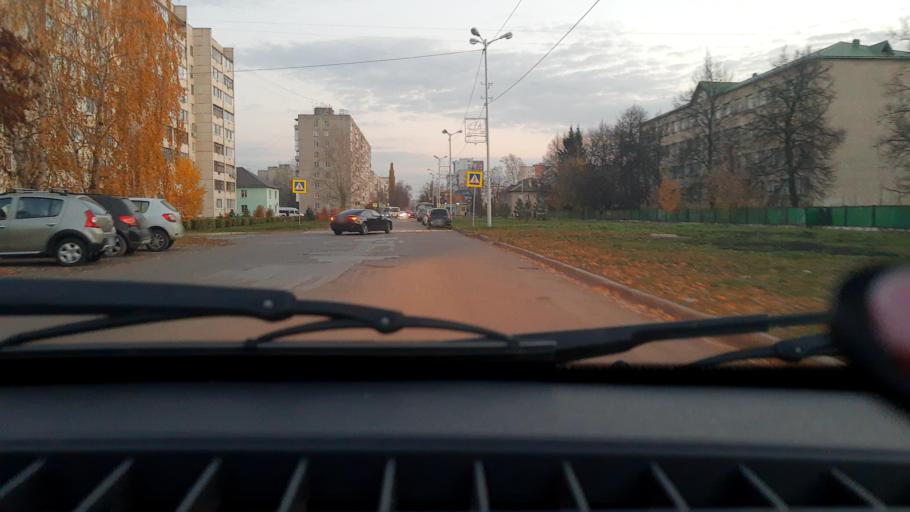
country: RU
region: Bashkortostan
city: Mikhaylovka
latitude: 54.7111
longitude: 55.8270
